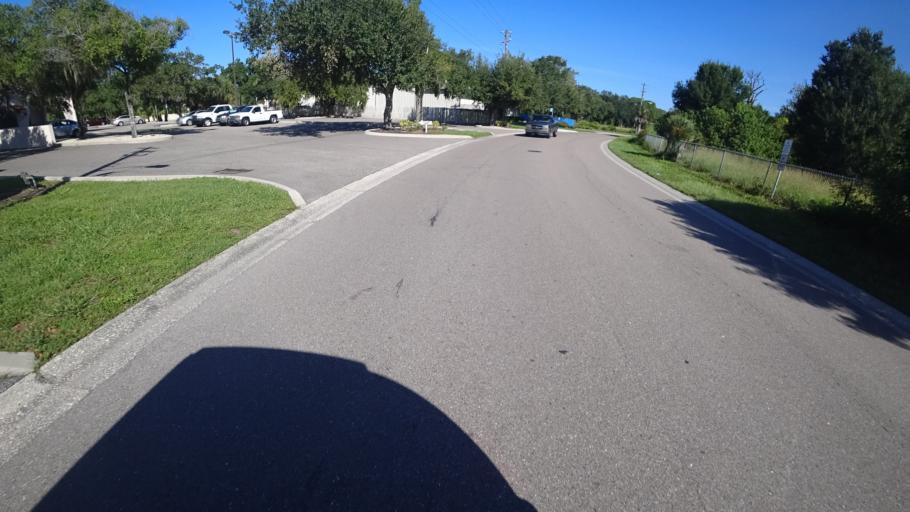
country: US
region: Florida
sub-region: Manatee County
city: Whitfield
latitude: 27.4248
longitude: -82.5372
